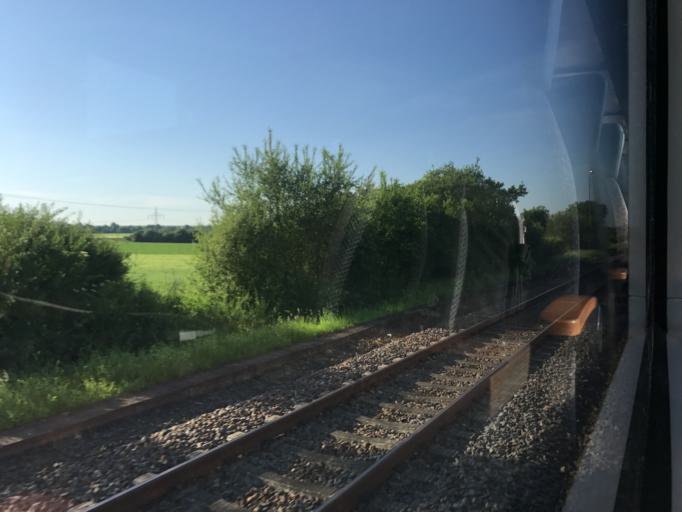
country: DE
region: Rheinland-Pfalz
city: Gensingen
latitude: 49.9066
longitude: 7.9397
